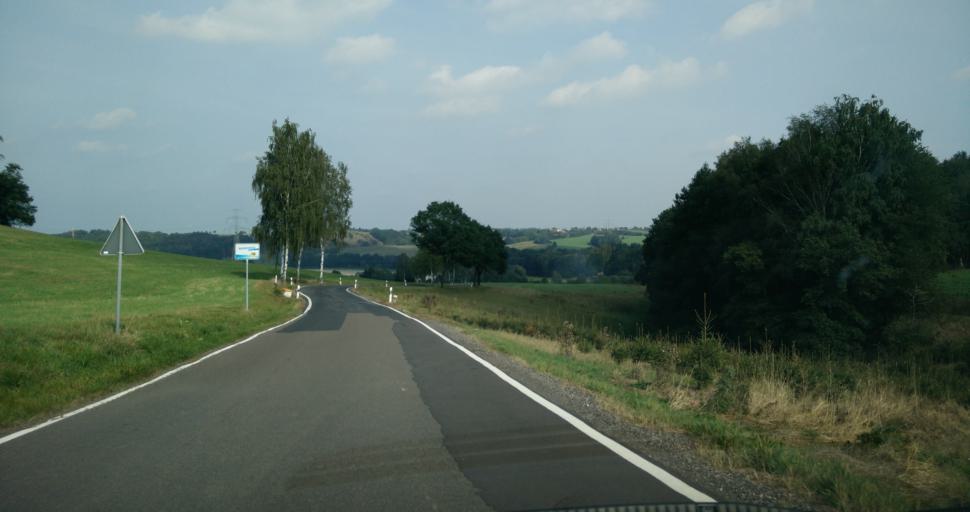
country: DE
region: Saxony
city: Colditz
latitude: 51.1030
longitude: 12.8010
